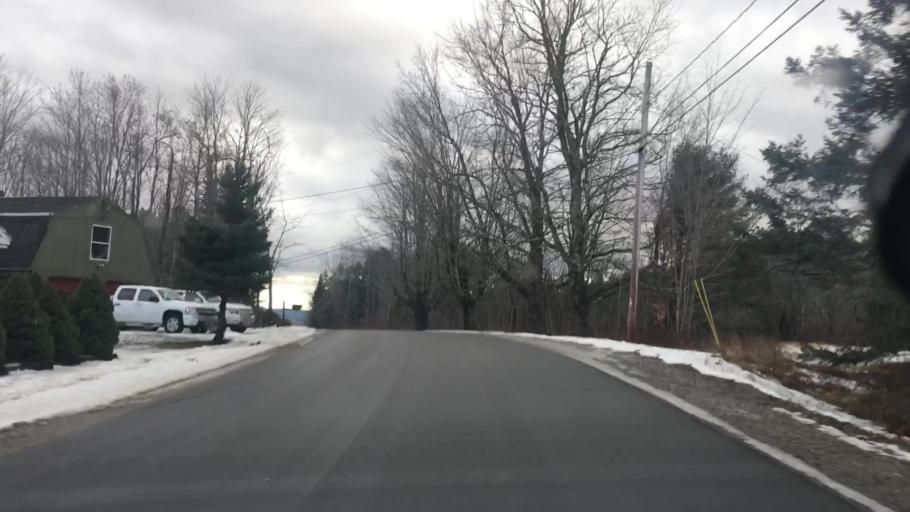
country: US
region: Maine
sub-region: Hancock County
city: Dedham
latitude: 44.6595
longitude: -68.7049
